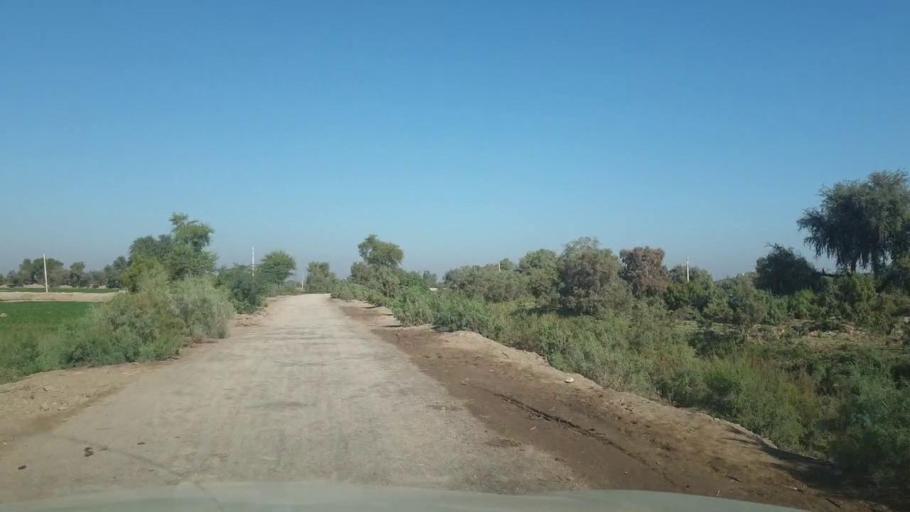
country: PK
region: Sindh
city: Bhan
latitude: 26.5389
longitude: 67.6582
